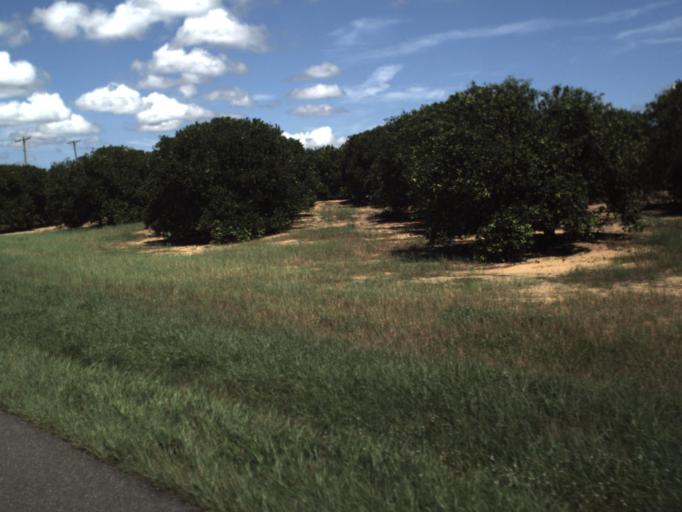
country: US
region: Florida
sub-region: Polk County
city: Crooked Lake Park
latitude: 27.8440
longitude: -81.5715
